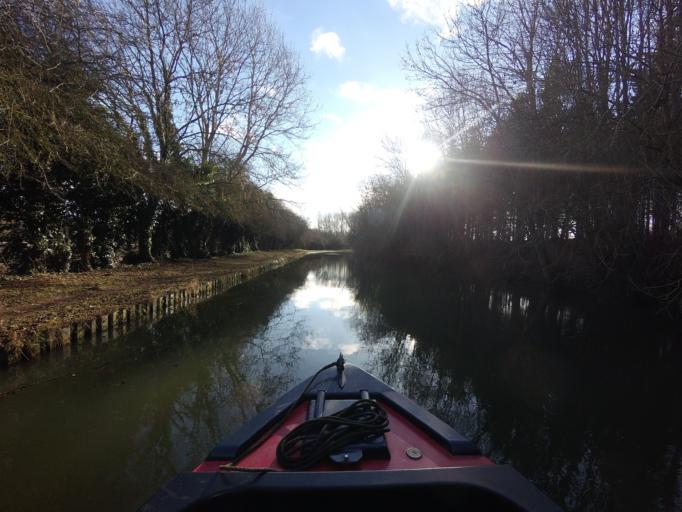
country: GB
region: England
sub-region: Northamptonshire
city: Long Buckby
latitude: 52.2619
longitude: -1.0891
